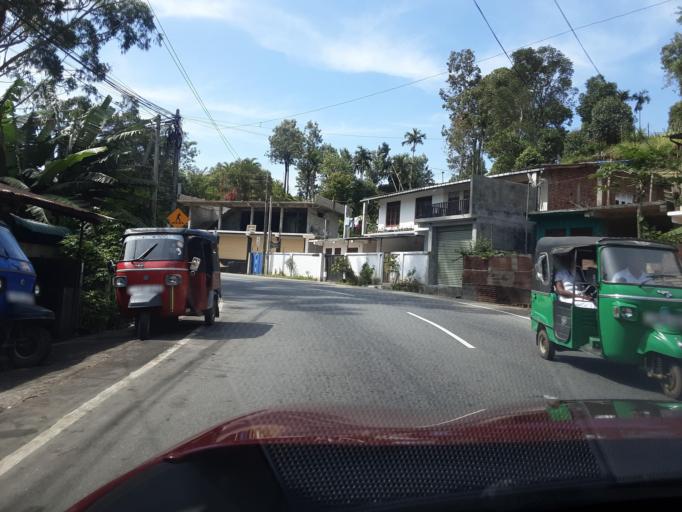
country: LK
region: Uva
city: Badulla
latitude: 6.9556
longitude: 81.1203
